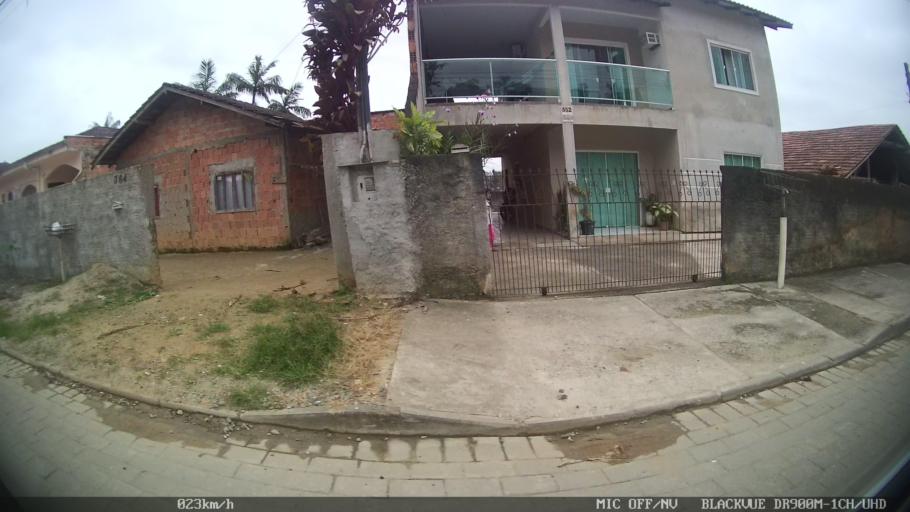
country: BR
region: Santa Catarina
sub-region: Joinville
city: Joinville
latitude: -26.3494
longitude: -48.8267
